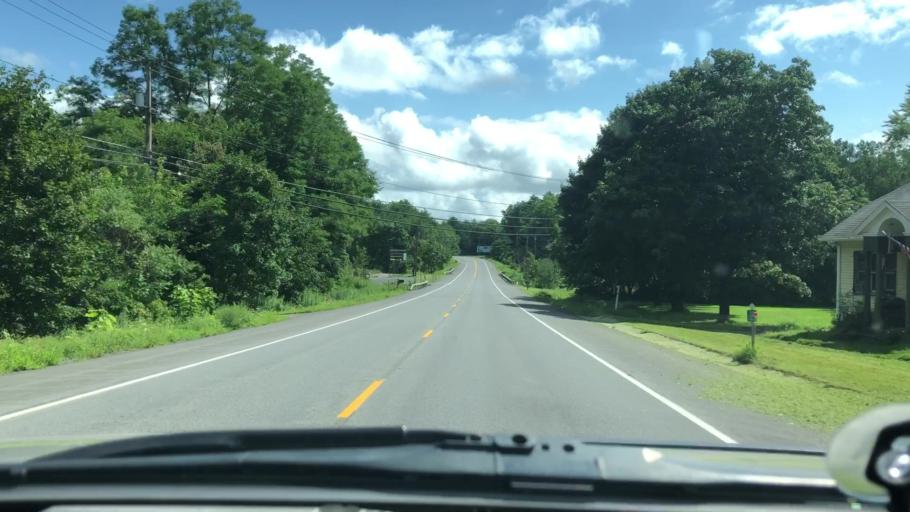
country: US
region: New York
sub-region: Greene County
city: Cairo
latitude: 42.3037
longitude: -74.0284
